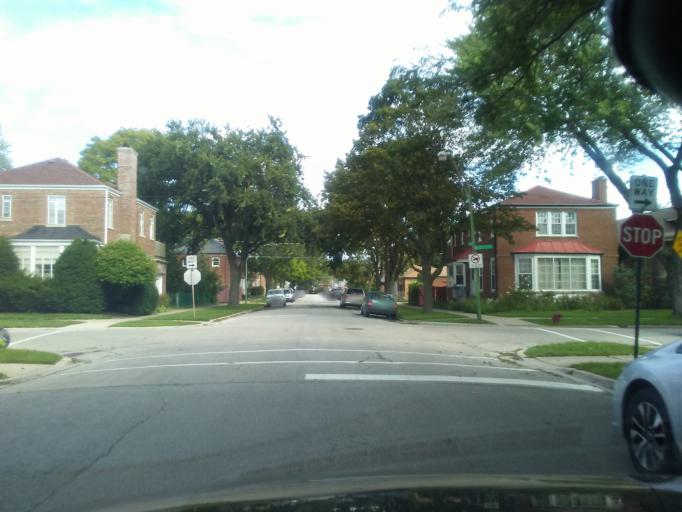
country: US
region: Illinois
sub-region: Cook County
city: Lincolnwood
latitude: 42.0101
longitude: -87.7021
